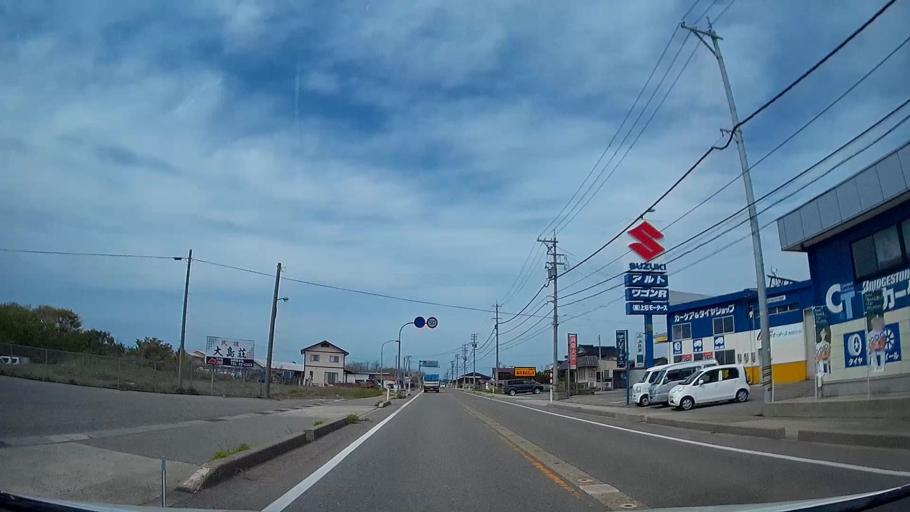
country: JP
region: Ishikawa
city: Hakui
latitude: 36.9882
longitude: 136.7761
